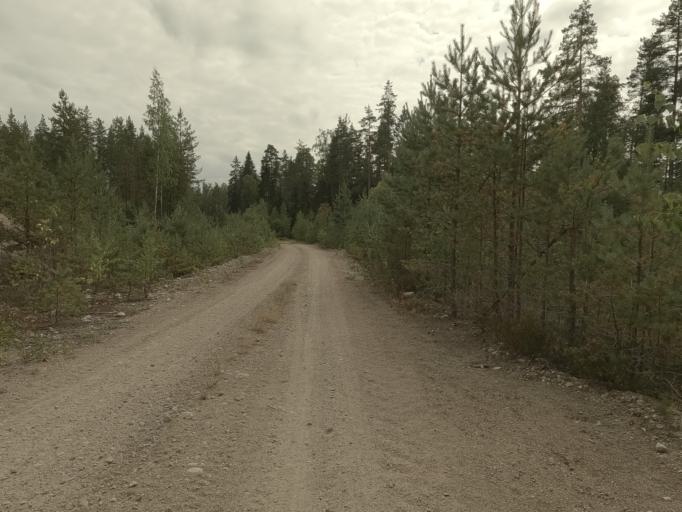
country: RU
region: Leningrad
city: Kamennogorsk
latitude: 61.0204
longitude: 29.1899
